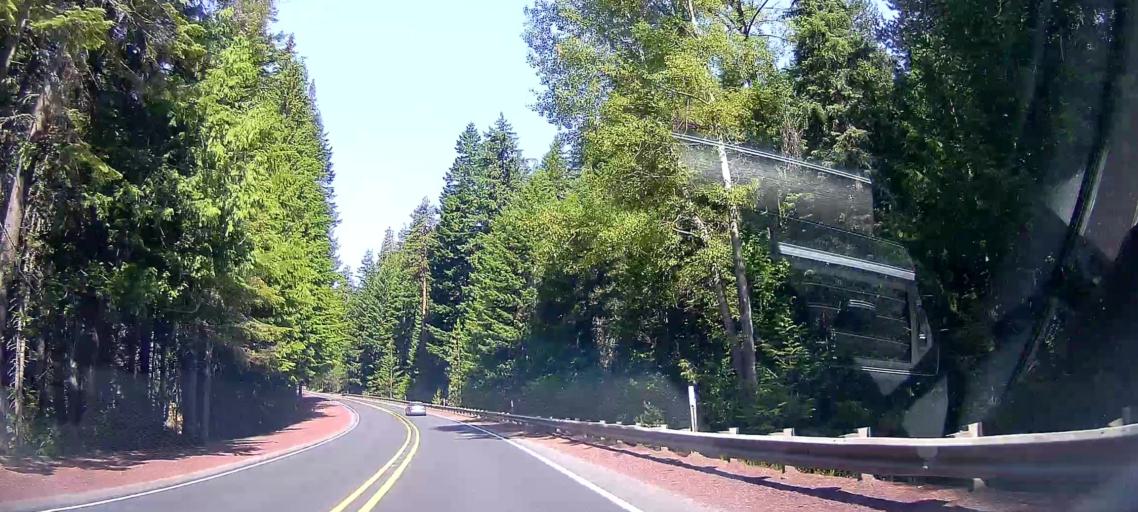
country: US
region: Oregon
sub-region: Clackamas County
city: Mount Hood Village
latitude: 45.1258
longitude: -121.5893
